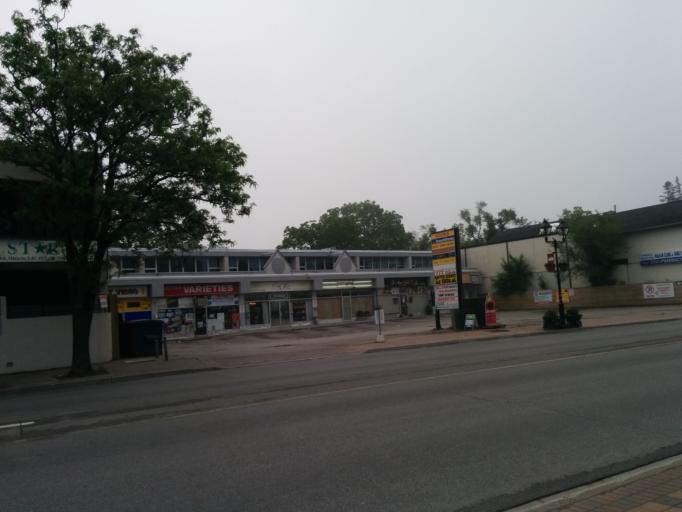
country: CA
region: Ontario
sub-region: York
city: Richmond Hill
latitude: 43.8777
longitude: -79.4389
